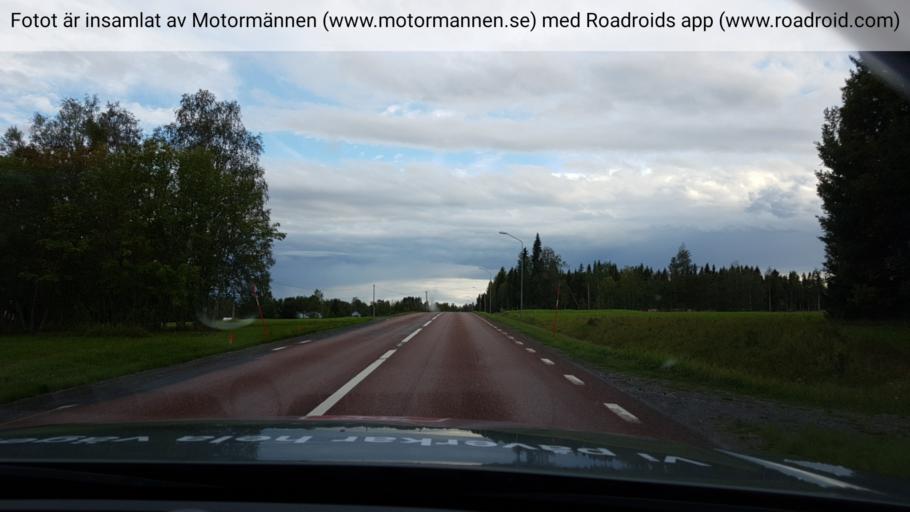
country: SE
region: Jaemtland
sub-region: Stroemsunds Kommun
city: Stroemsund
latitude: 63.7402
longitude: 15.4899
